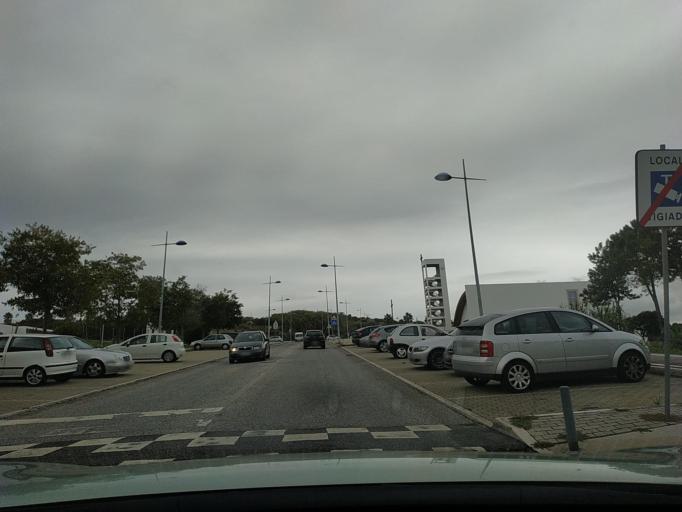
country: PT
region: Lisbon
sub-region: Amadora
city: Amadora
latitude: 38.7685
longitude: -9.2350
